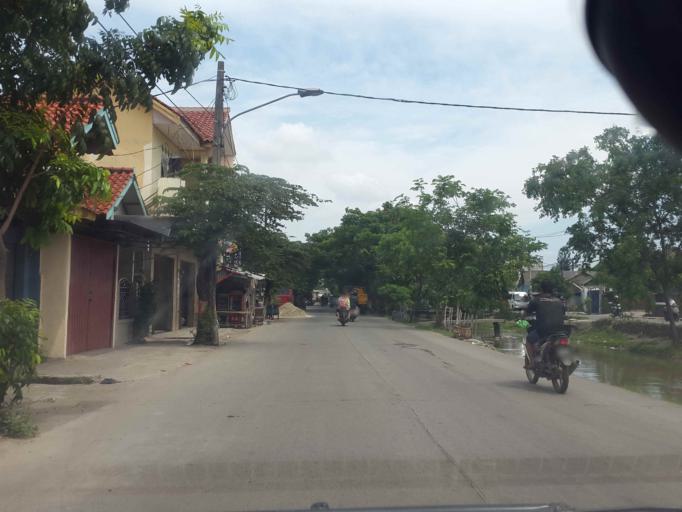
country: ID
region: Banten
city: Tangerang
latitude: -6.1545
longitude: 106.6722
